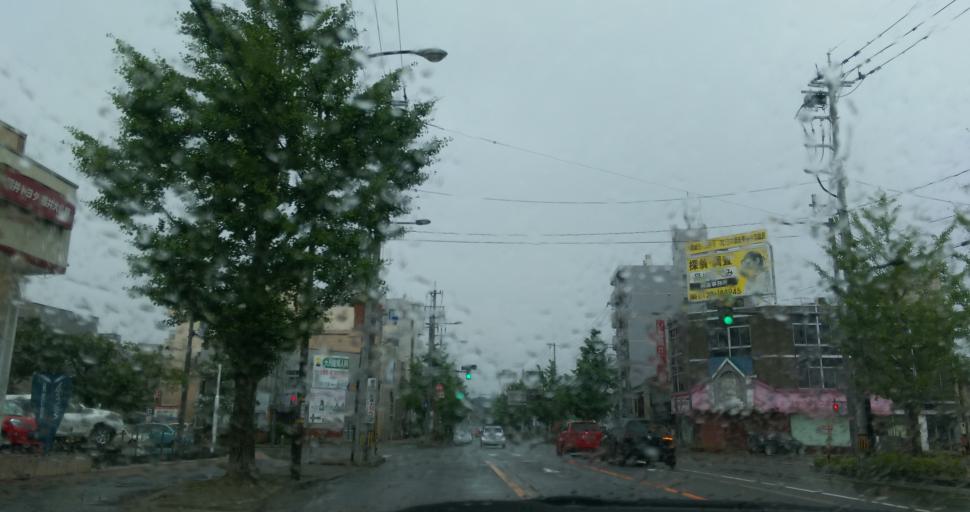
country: JP
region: Fukui
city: Fukui-shi
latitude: 36.0679
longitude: 136.2125
